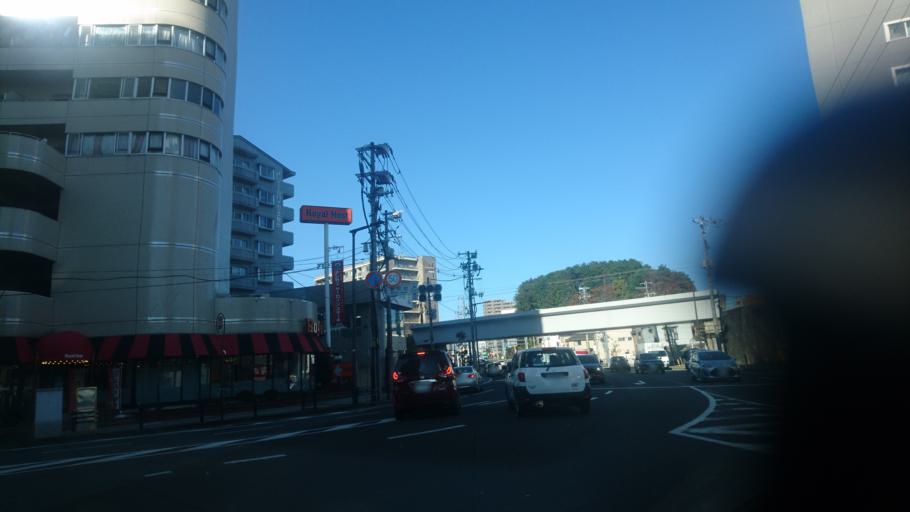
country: JP
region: Miyagi
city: Sendai-shi
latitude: 38.2799
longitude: 140.8725
